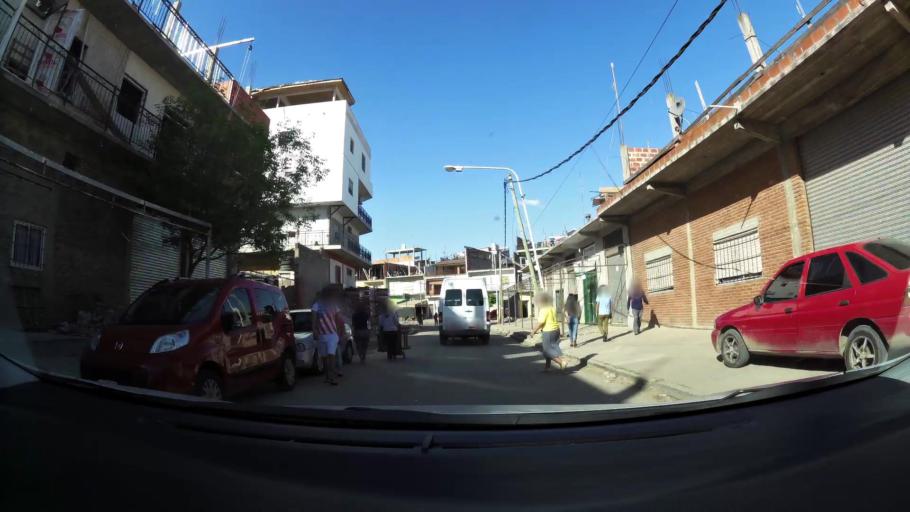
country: AR
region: Buenos Aires F.D.
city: Villa Lugano
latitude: -34.7029
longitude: -58.4820
